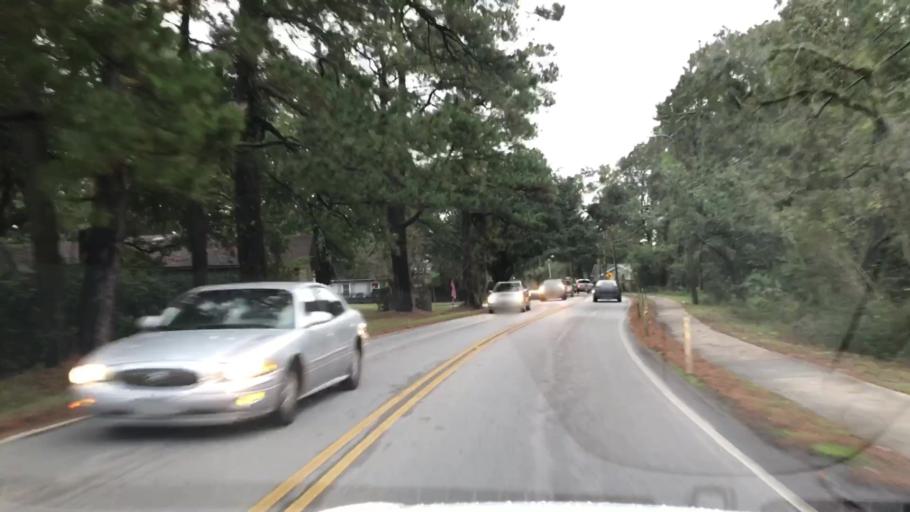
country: US
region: South Carolina
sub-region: Charleston County
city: North Charleston
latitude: 32.8153
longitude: -80.0152
